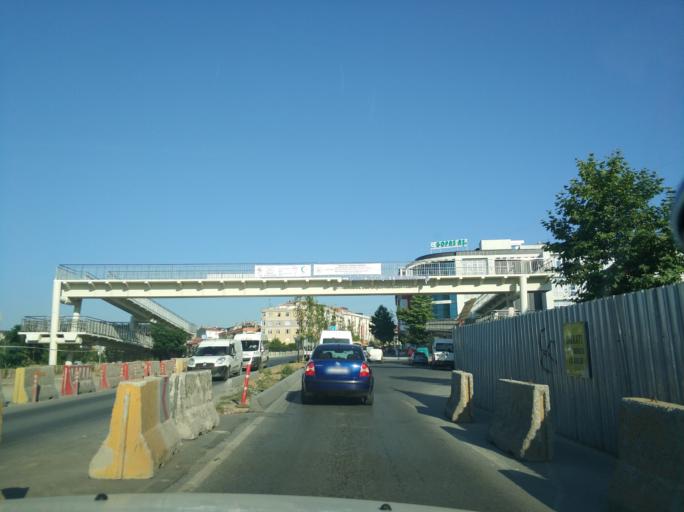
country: TR
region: Istanbul
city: Sultangazi
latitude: 41.0847
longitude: 28.9099
